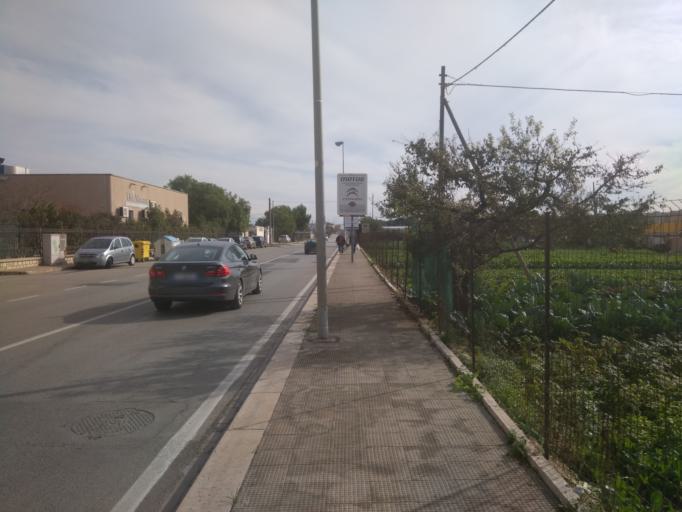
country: IT
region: Apulia
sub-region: Provincia di Bari
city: Bari
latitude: 41.1126
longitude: 16.8994
